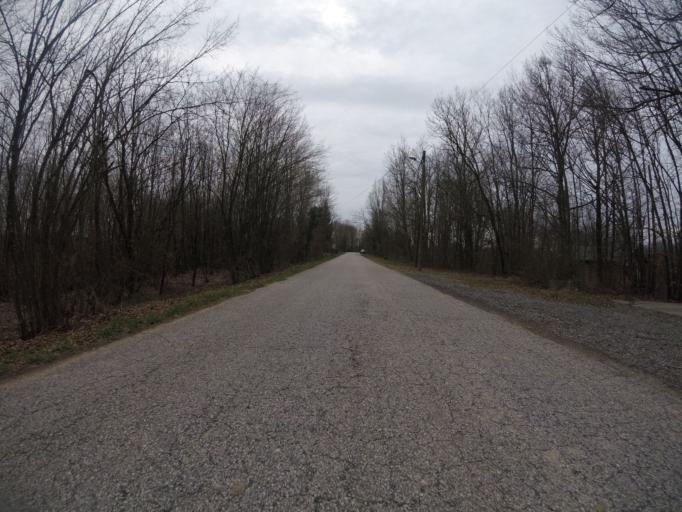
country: HR
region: Zagrebacka
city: Lukavec
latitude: 45.5834
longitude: 15.9644
